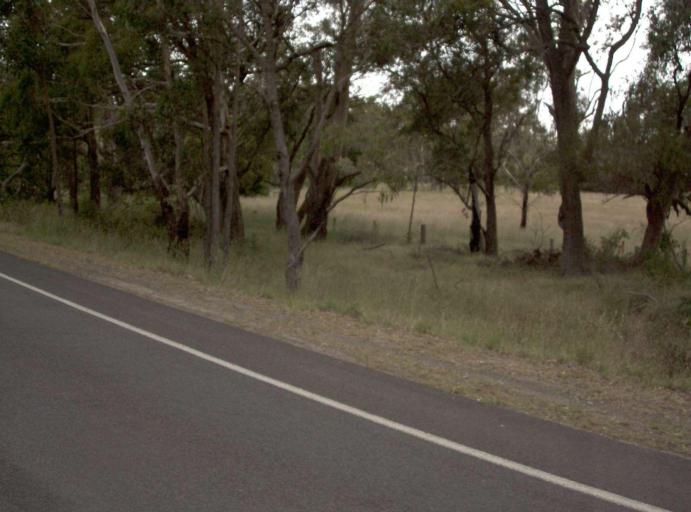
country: AU
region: Victoria
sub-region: Wellington
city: Sale
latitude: -38.5270
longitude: 146.8693
